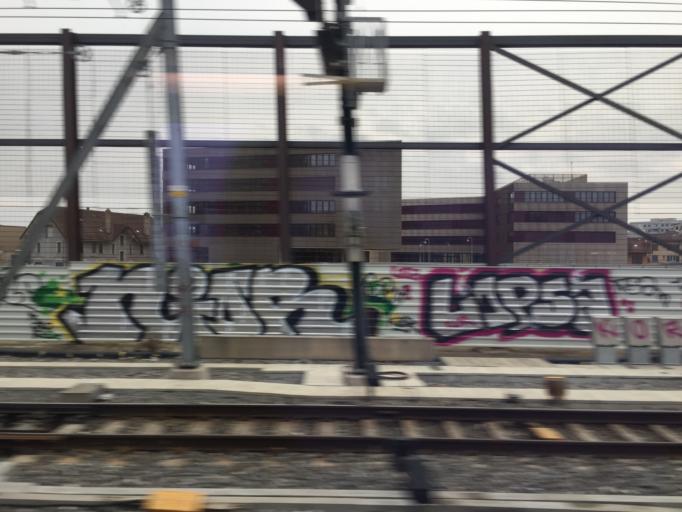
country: CH
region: Vaud
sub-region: Ouest Lausannois District
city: Renens
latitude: 46.5347
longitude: 6.5845
